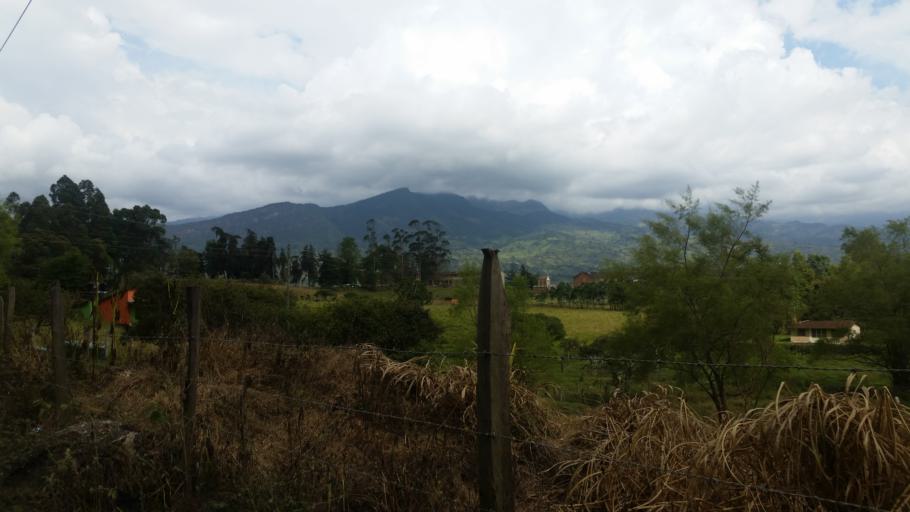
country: CO
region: Cundinamarca
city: Choachi
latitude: 4.5221
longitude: -73.9286
